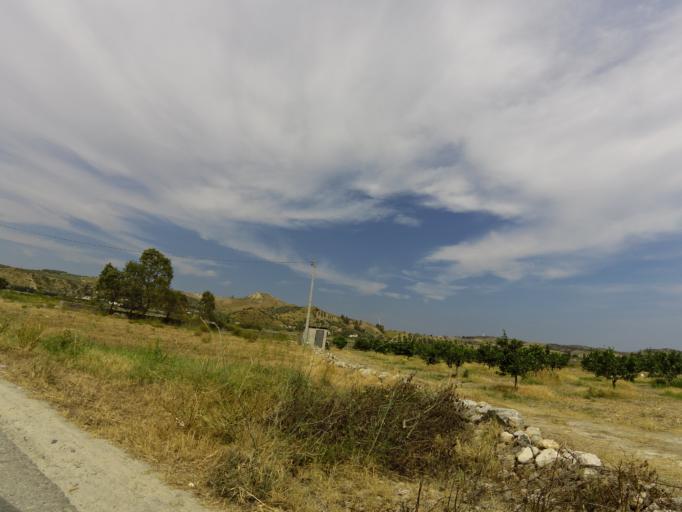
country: IT
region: Calabria
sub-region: Provincia di Reggio Calabria
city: Monasterace
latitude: 38.4496
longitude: 16.5214
